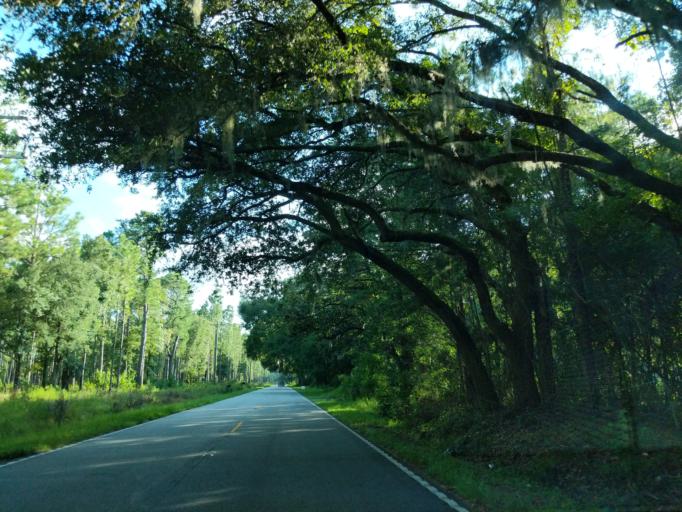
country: US
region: South Carolina
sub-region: Charleston County
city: Awendaw
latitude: 33.1460
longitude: -79.4171
